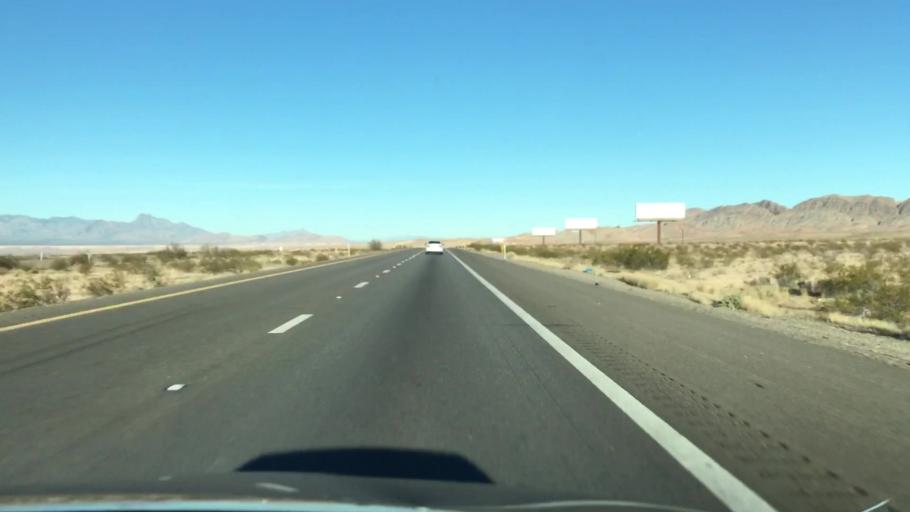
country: US
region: Nevada
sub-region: Clark County
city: Moapa Town
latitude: 36.5722
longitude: -114.6674
